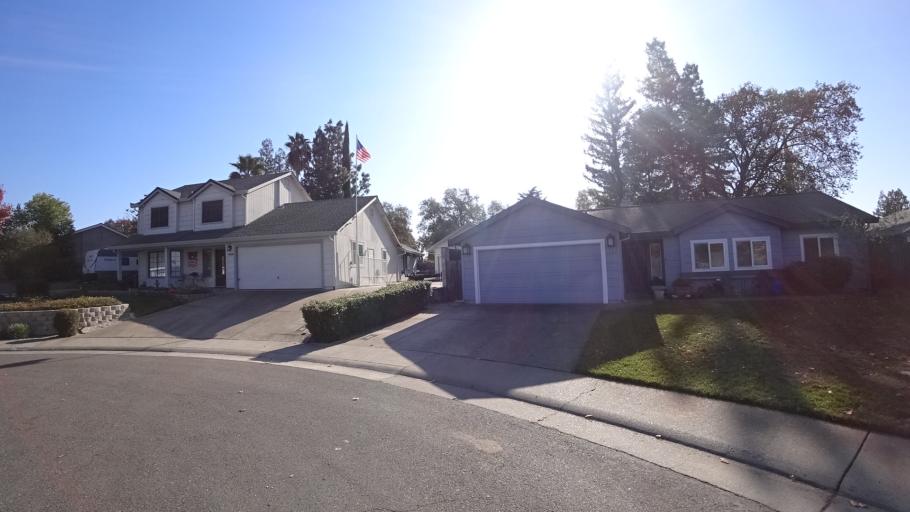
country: US
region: California
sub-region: Sacramento County
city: Citrus Heights
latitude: 38.6949
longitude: -121.2867
